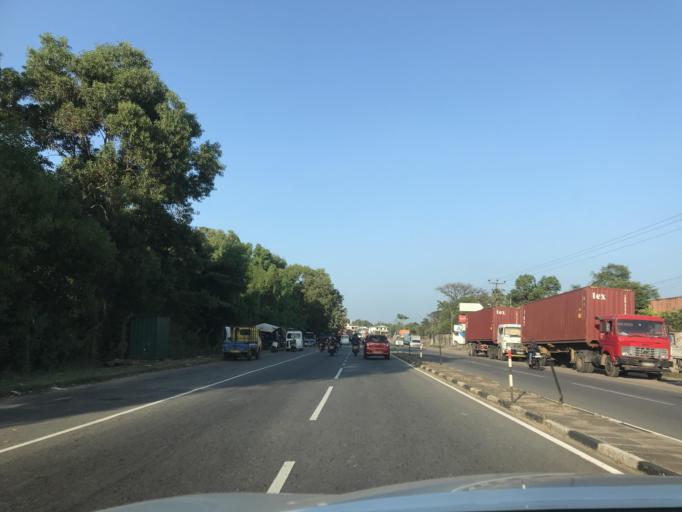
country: LK
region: Western
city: Ja Ela
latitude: 7.0986
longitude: 79.9081
